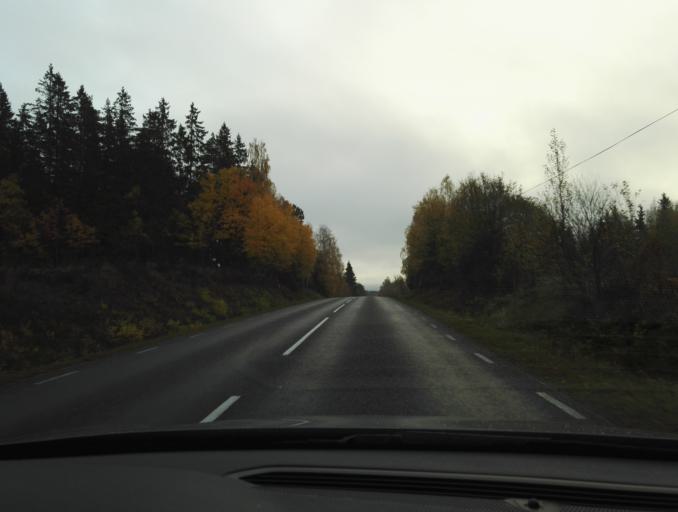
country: SE
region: Kronoberg
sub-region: Alvesta Kommun
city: Moheda
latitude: 57.0086
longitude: 14.7229
